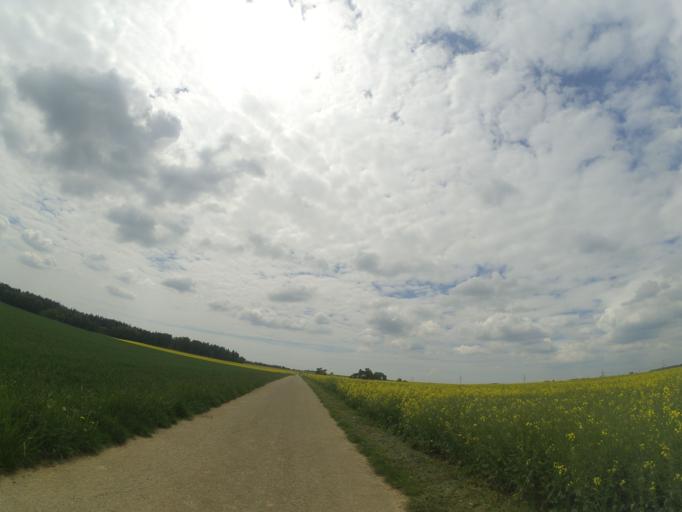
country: DE
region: Baden-Wuerttemberg
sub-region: Tuebingen Region
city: Blaubeuren
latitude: 48.4273
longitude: 9.8294
